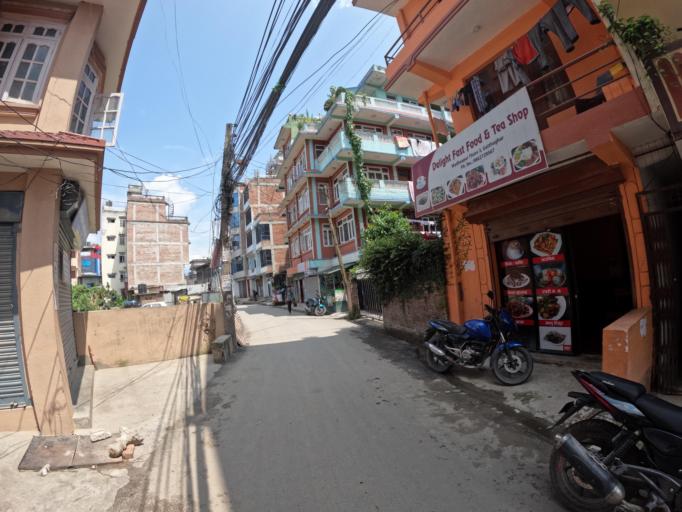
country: NP
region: Central Region
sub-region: Bagmati Zone
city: Bhaktapur
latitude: 27.6732
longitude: 85.3733
